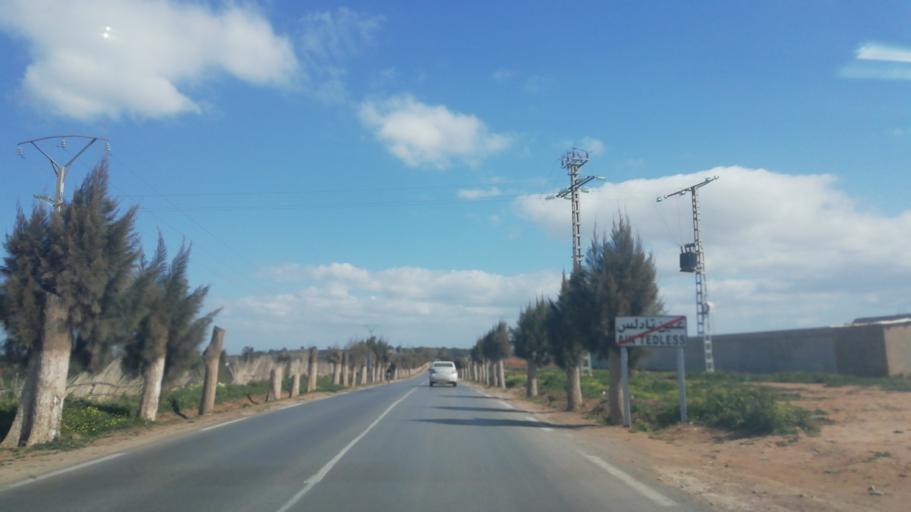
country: DZ
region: Mostaganem
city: Mostaganem
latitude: 35.9996
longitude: 0.3084
